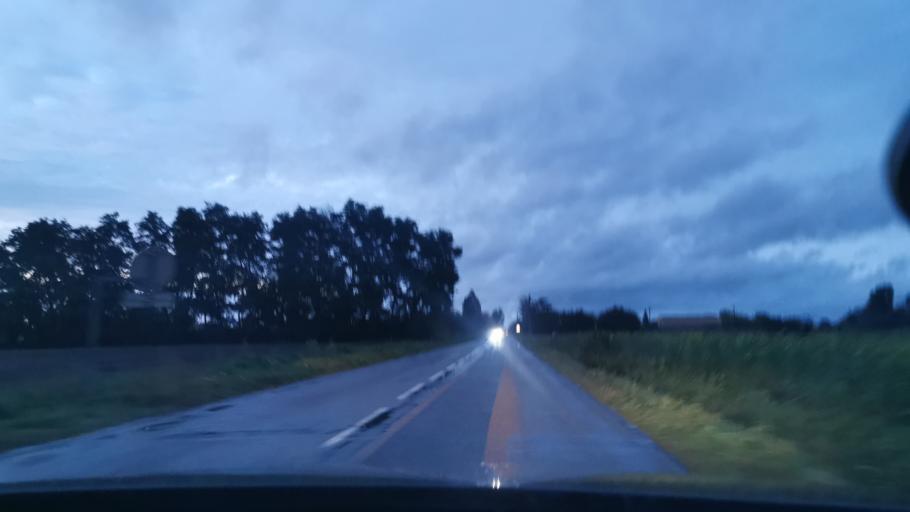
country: FR
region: Rhone-Alpes
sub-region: Departement de l'Ain
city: Bage-la-Ville
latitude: 46.3307
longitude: 4.9363
